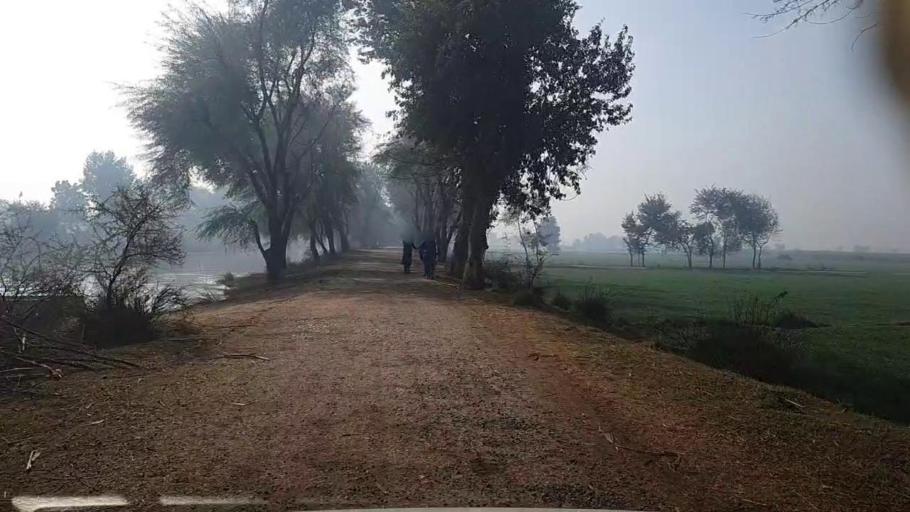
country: PK
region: Sindh
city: Khairpur
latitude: 27.9566
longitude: 69.6535
